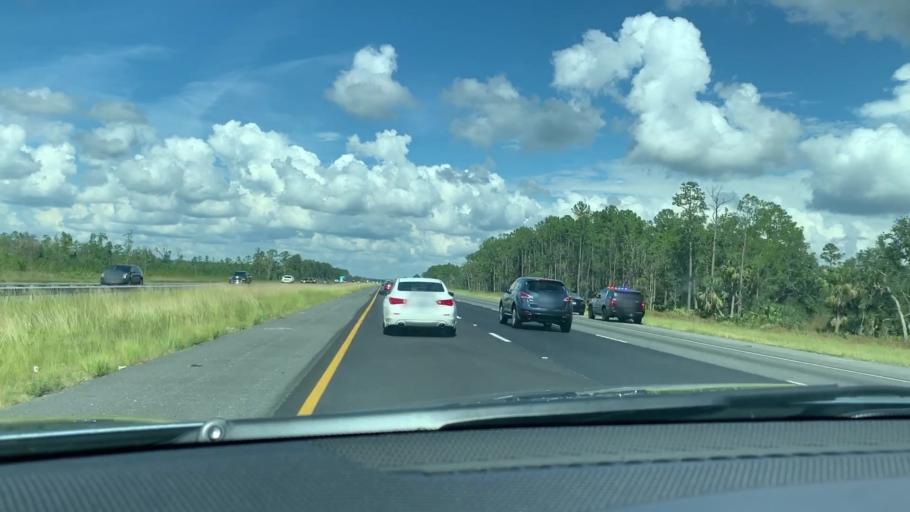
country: US
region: Georgia
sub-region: Camden County
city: Woodbine
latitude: 30.9985
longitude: -81.6638
